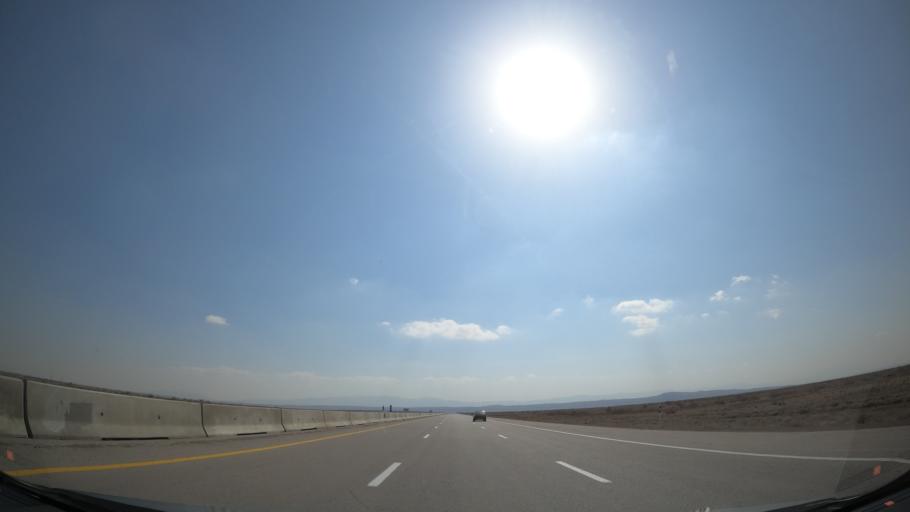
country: IR
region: Alborz
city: Nazarabad
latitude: 35.8604
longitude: 50.4797
